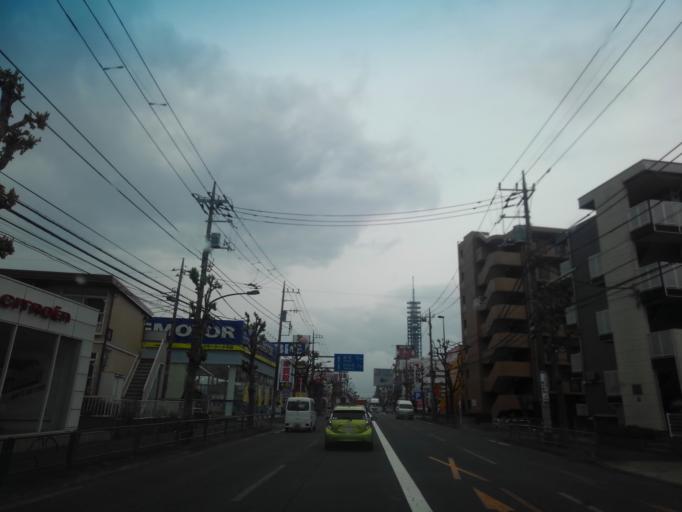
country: JP
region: Tokyo
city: Tanashicho
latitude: 35.7377
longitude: 139.5153
